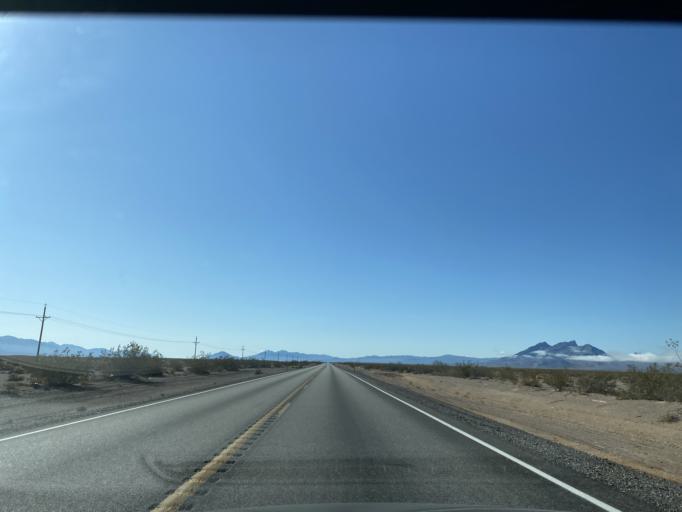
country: US
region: Nevada
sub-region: Nye County
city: Pahrump
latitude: 36.4904
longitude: -116.4214
